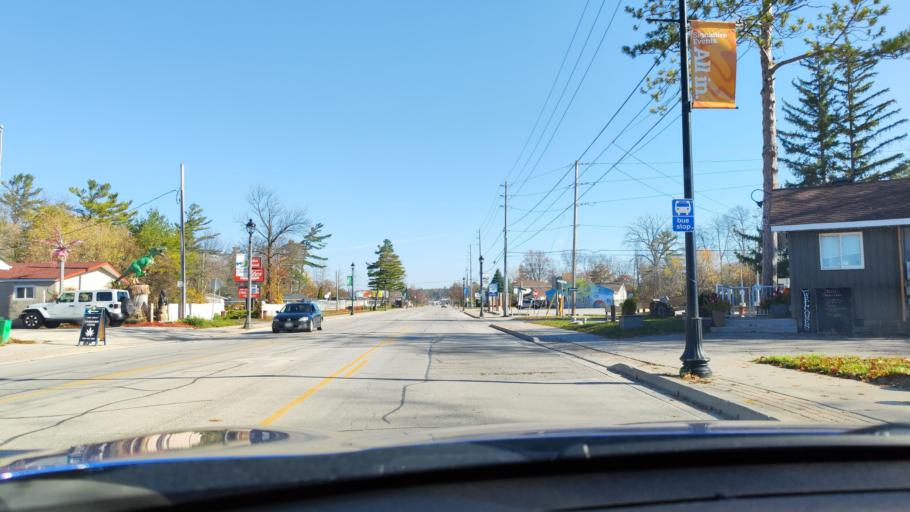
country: CA
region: Ontario
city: Wasaga Beach
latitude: 44.5226
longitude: -80.0148
